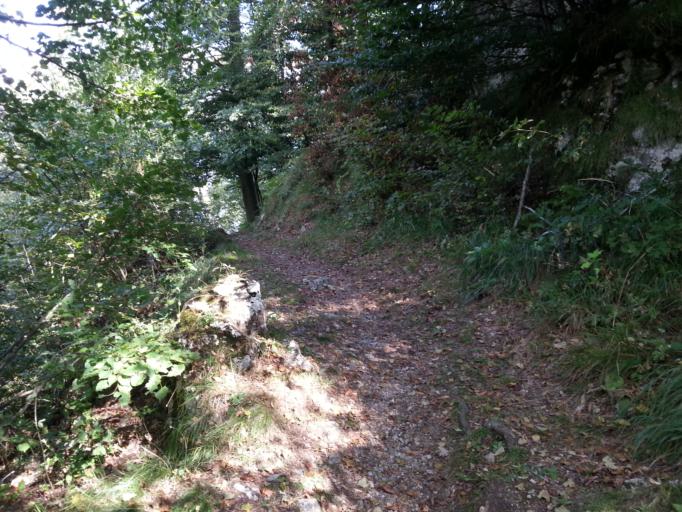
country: IT
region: Lombardy
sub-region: Provincia di Lecco
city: Pasturo
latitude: 45.9405
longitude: 9.4341
